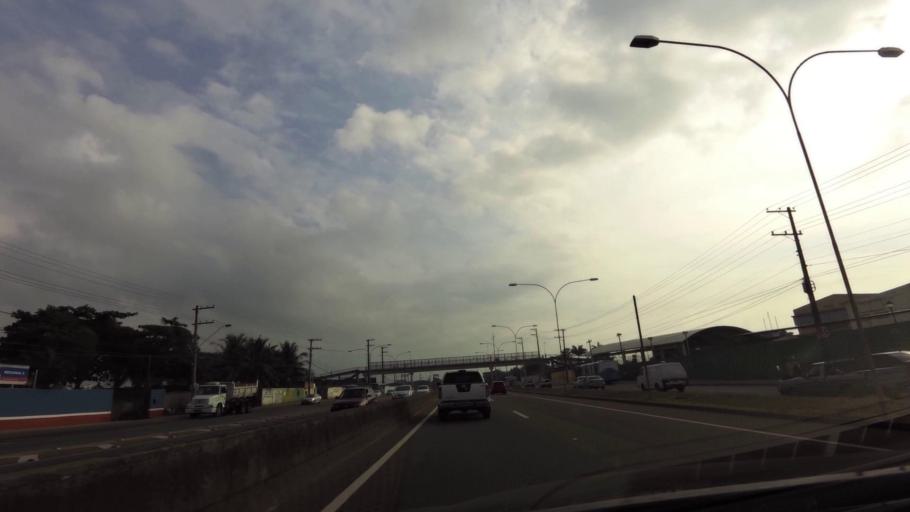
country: BR
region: Espirito Santo
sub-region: Vila Velha
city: Vila Velha
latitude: -20.4219
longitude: -40.3292
